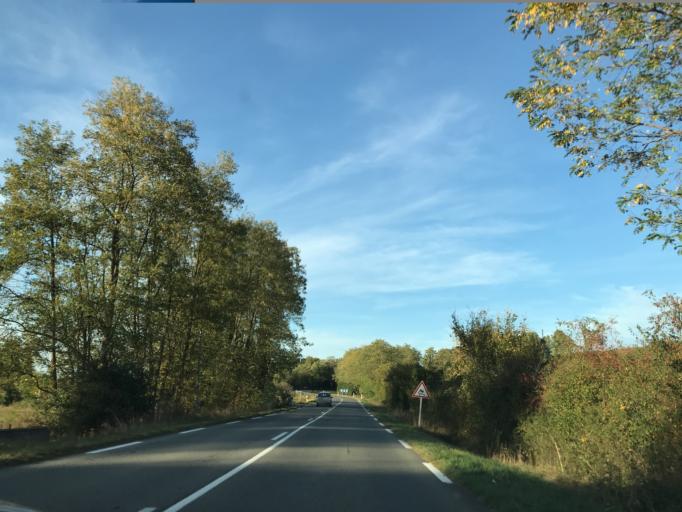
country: FR
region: Auvergne
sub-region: Departement du Puy-de-Dome
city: Puy-Guillaume
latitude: 45.9840
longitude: 3.4850
